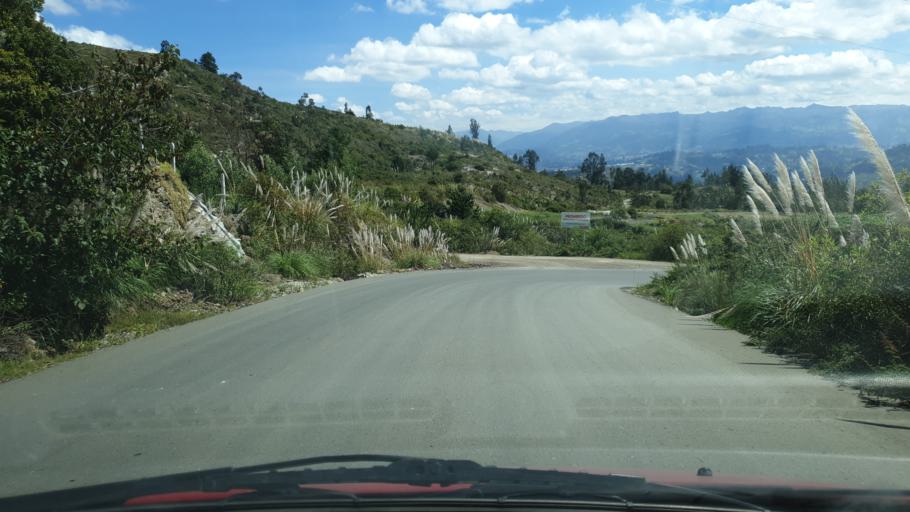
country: EC
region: Azuay
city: Llacao
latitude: -2.8776
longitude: -78.8978
